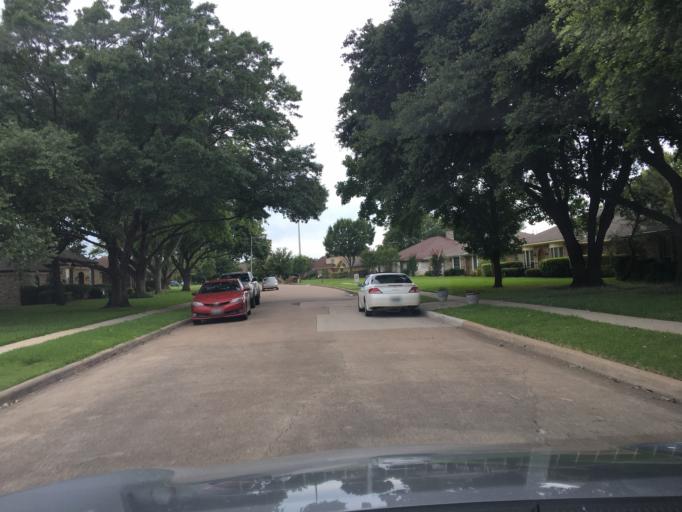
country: US
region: Texas
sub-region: Dallas County
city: Richardson
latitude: 32.9433
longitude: -96.7111
